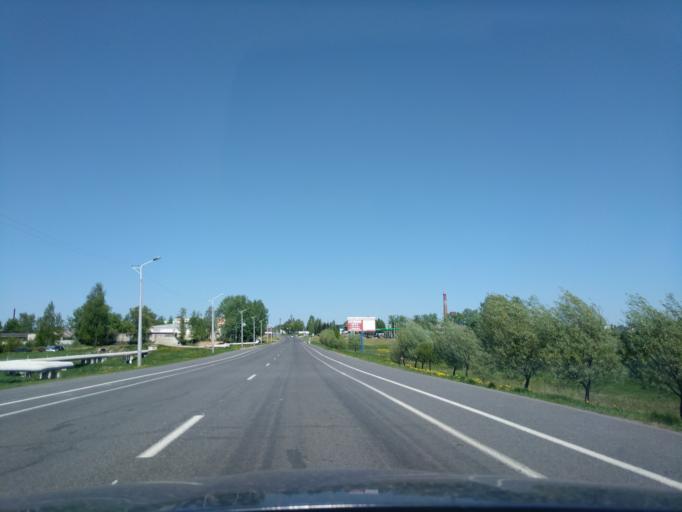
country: BY
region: Minsk
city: Myadzyel
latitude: 54.8802
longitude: 26.9398
